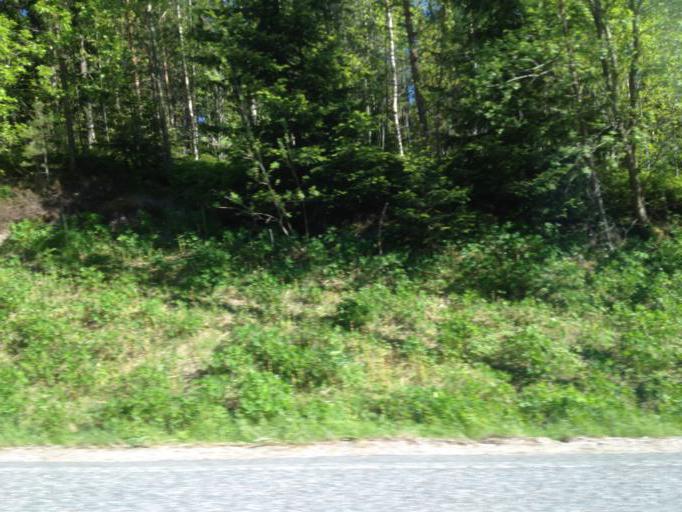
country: FI
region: Uusimaa
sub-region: Helsinki
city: Espoo
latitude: 60.2584
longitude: 24.6006
